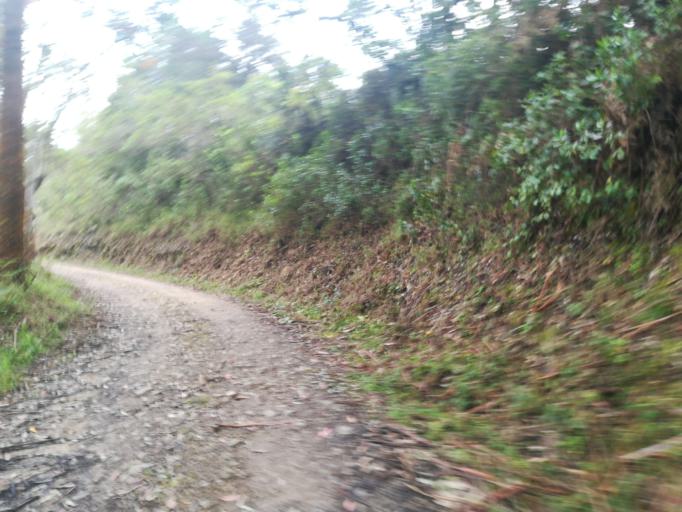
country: CO
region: Cundinamarca
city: Tenza
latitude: 5.0626
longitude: -73.4594
